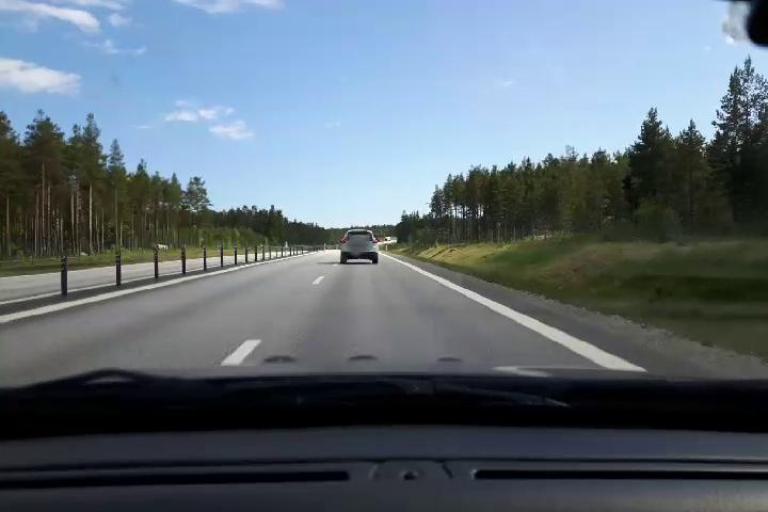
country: SE
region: Gaevleborg
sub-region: Hudiksvalls Kommun
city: Hudiksvall
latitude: 61.7034
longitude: 17.0528
